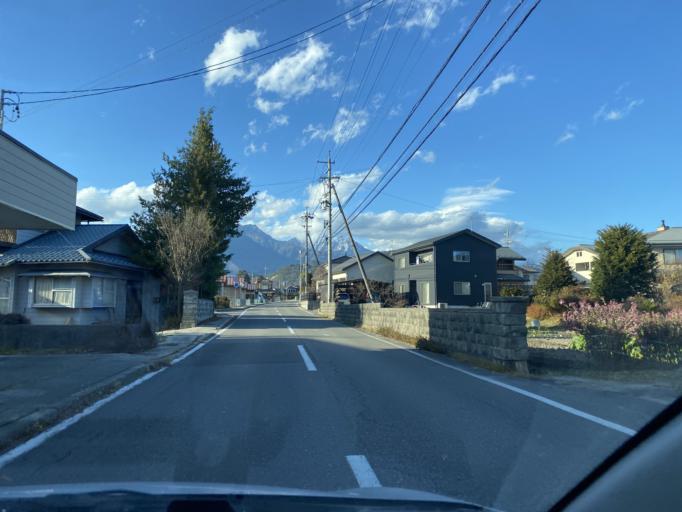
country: JP
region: Nagano
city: Omachi
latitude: 36.5174
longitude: 137.8417
